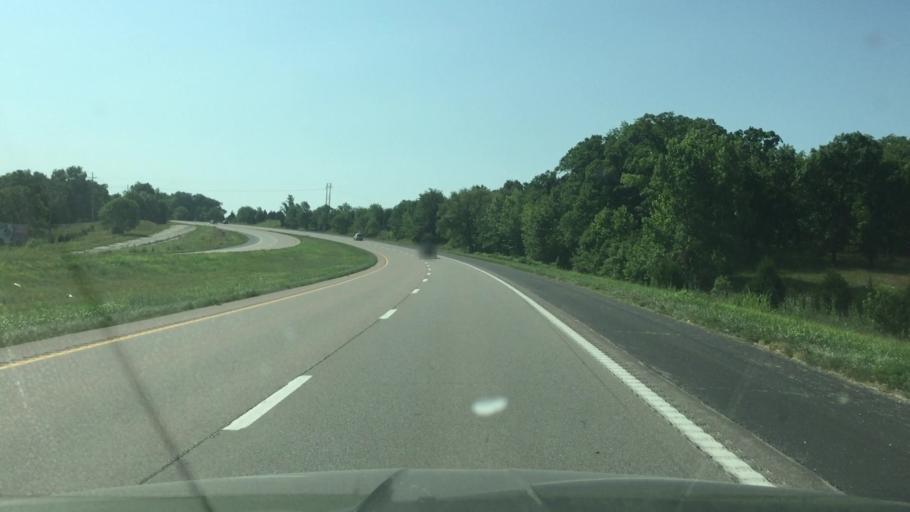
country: US
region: Missouri
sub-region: Pettis County
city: Sedalia
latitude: 38.7228
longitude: -93.3010
